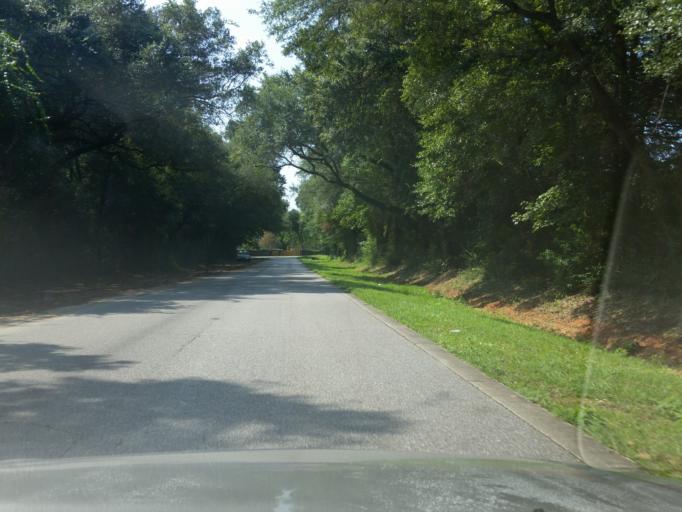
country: US
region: Florida
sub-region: Escambia County
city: Bellview
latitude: 30.4600
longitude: -87.3329
